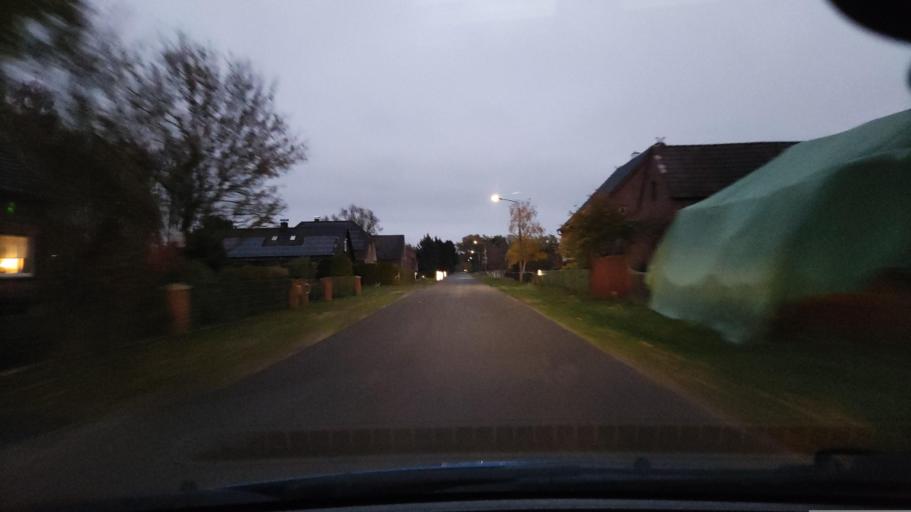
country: DE
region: Mecklenburg-Vorpommern
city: Domitz
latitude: 53.1674
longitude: 11.2216
